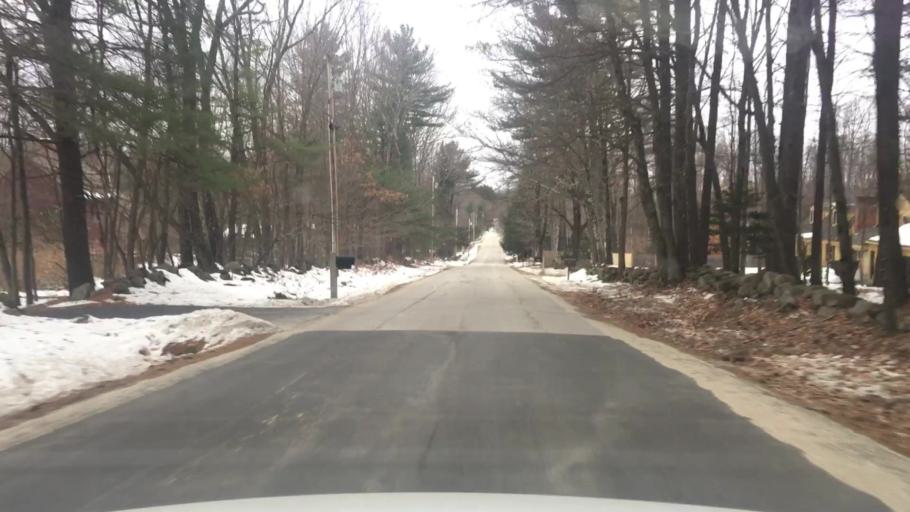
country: US
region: New Hampshire
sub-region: Merrimack County
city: Hopkinton
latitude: 43.1797
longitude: -71.6746
